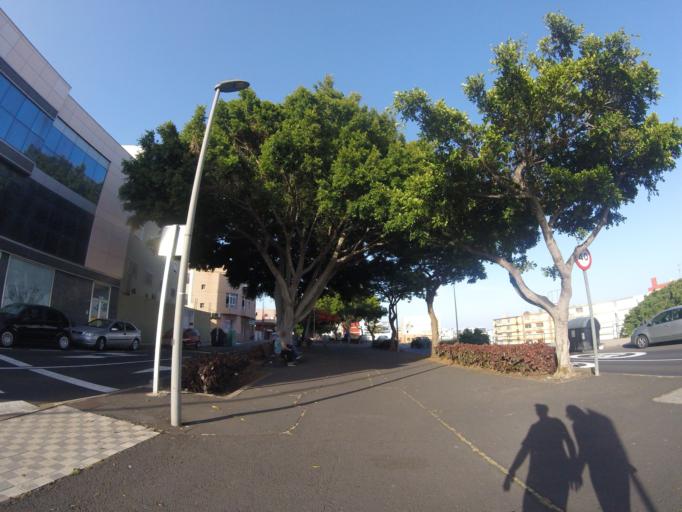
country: ES
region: Canary Islands
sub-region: Provincia de Santa Cruz de Tenerife
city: La Laguna
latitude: 28.4512
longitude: -16.3019
